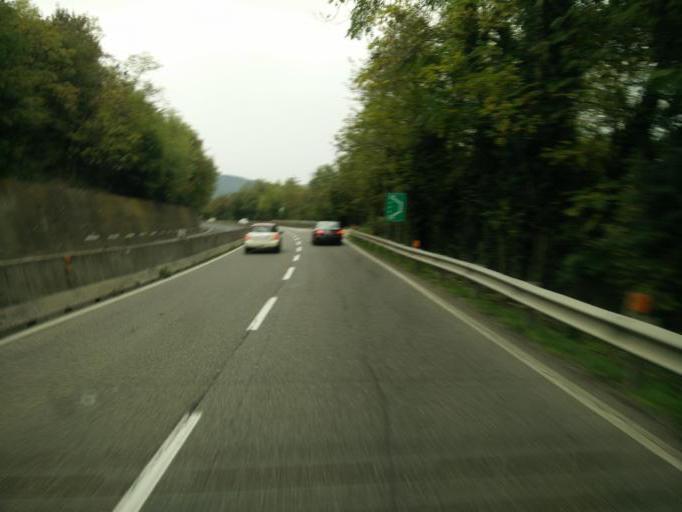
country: IT
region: Tuscany
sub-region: Province of Florence
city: San Casciano in Val di Pesa
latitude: 43.6584
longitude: 11.2017
